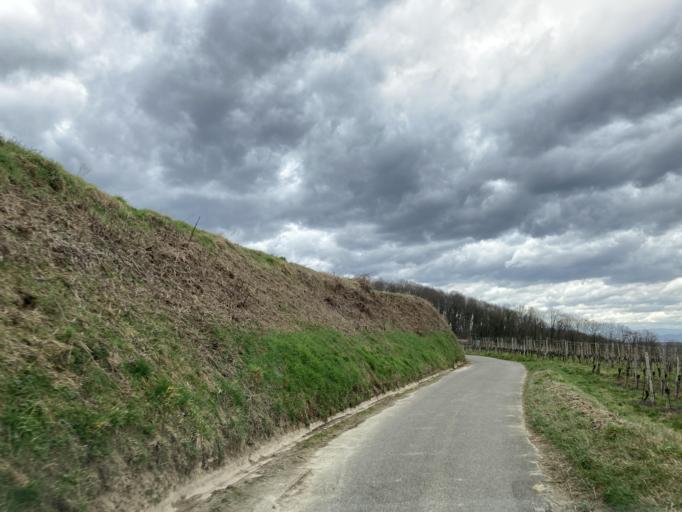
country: DE
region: Baden-Wuerttemberg
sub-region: Freiburg Region
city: Vogtsburg
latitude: 48.1194
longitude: 7.6468
